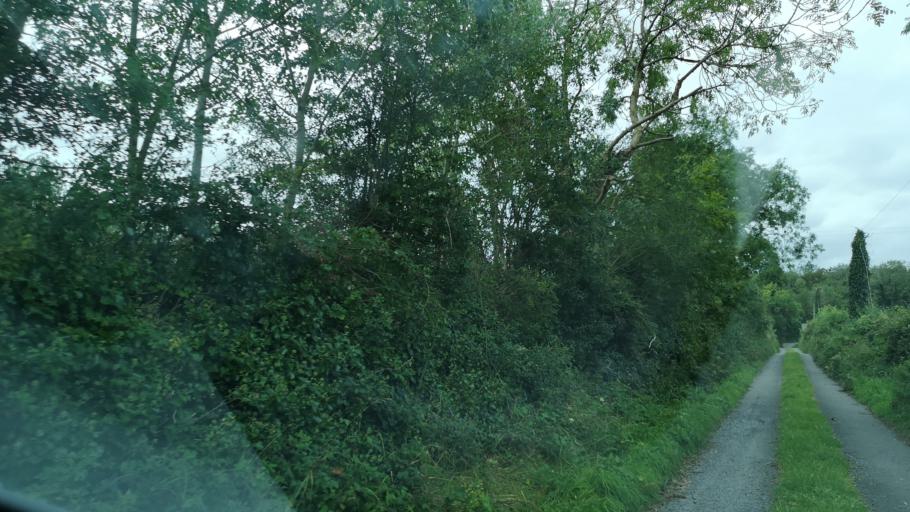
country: IE
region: Connaught
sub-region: County Galway
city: Loughrea
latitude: 53.1568
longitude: -8.4402
